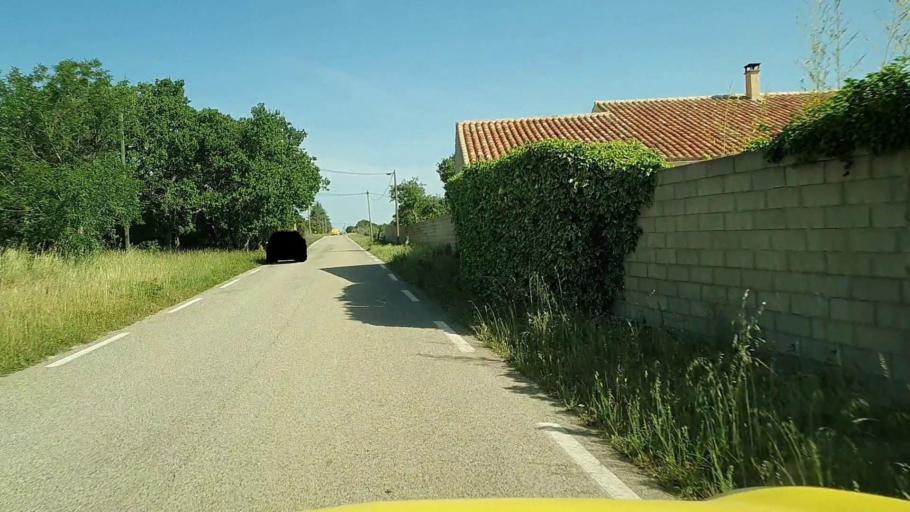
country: FR
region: Languedoc-Roussillon
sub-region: Departement du Gard
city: Montaren-et-Saint-Mediers
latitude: 44.1172
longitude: 4.3708
